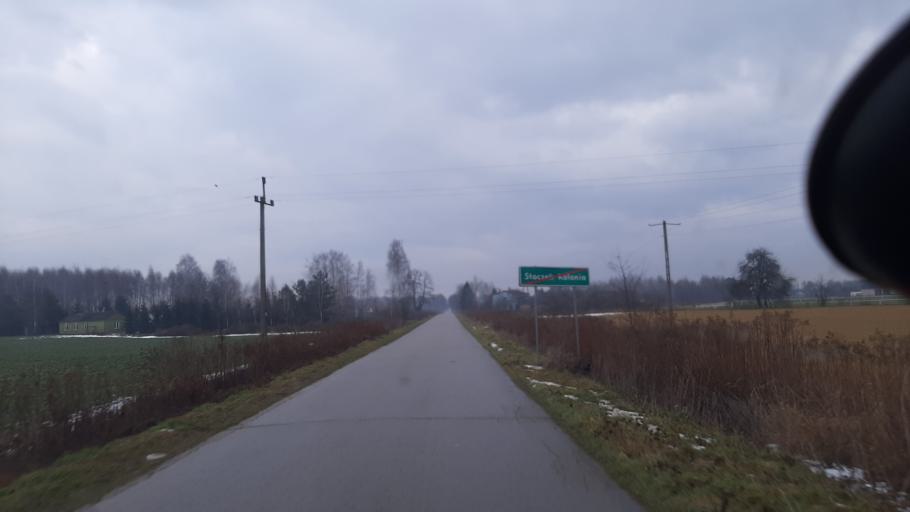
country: PL
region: Lublin Voivodeship
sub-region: Powiat lubelski
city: Lublin
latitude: 51.3382
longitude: 22.5416
